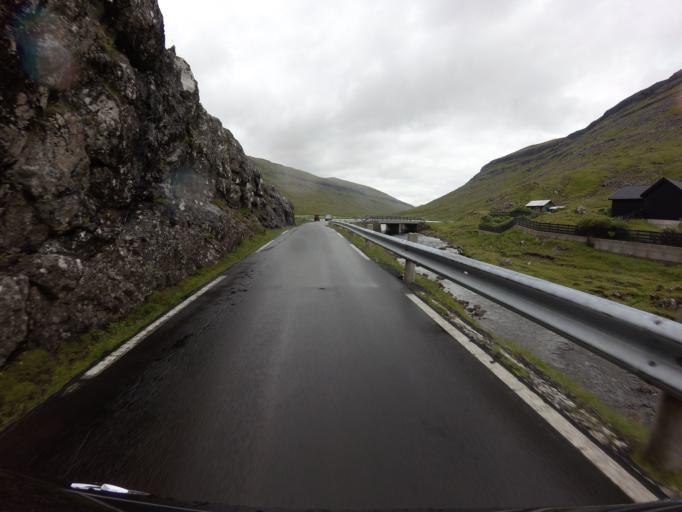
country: FO
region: Streymoy
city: Vestmanna
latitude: 62.2423
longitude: -7.1620
